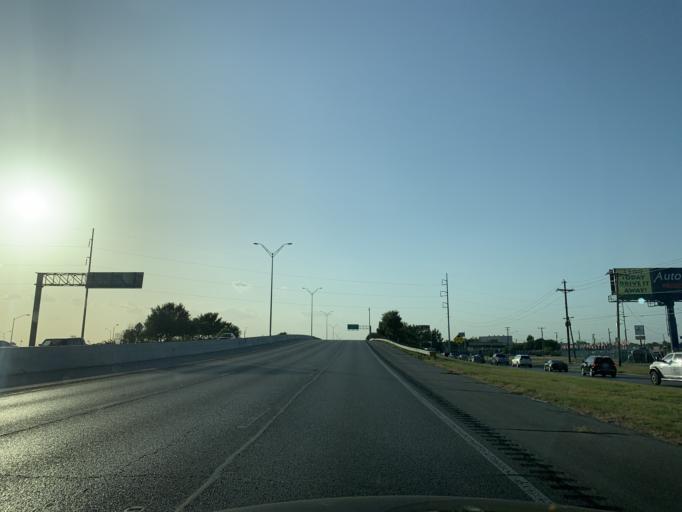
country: US
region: Texas
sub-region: Dallas County
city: Balch Springs
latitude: 32.7121
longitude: -96.6815
